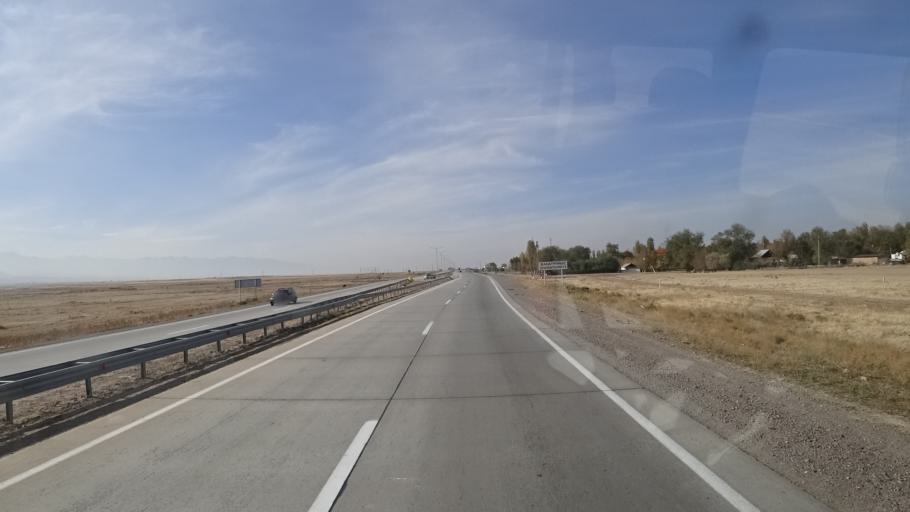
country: KZ
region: Zhambyl
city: Merke
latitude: 42.8884
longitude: 72.9963
